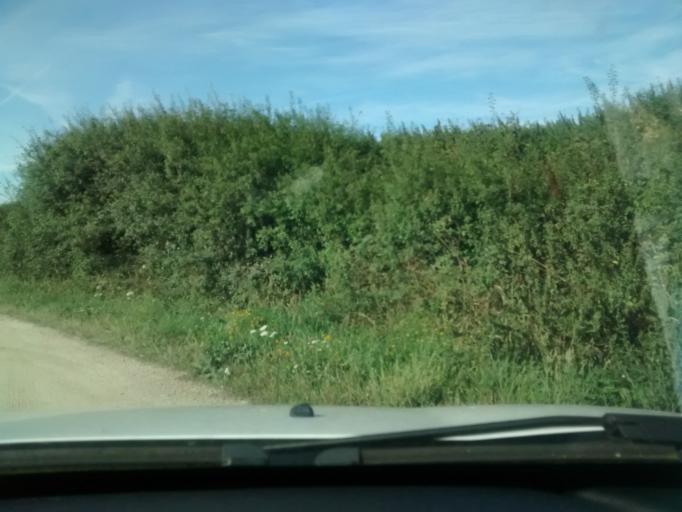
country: FR
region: Brittany
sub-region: Departement des Cotes-d'Armor
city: Plougrescant
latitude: 48.8665
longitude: -3.2318
